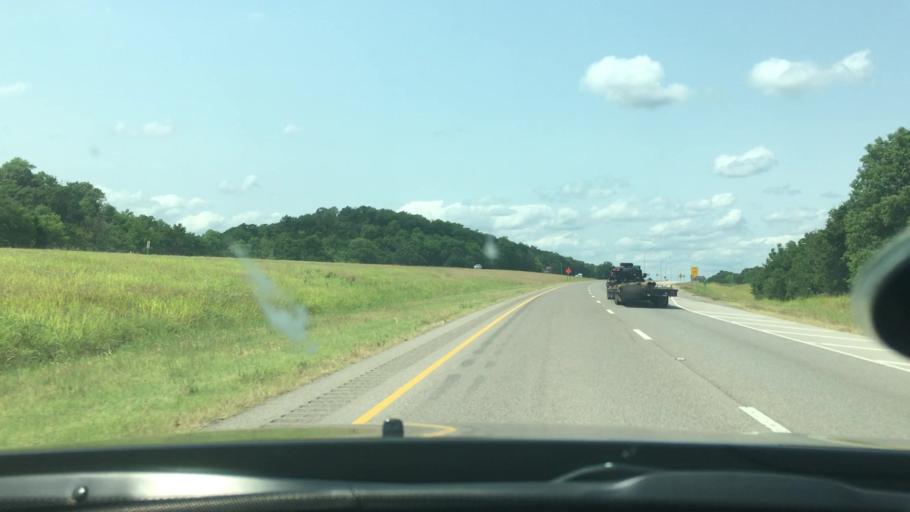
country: US
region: Oklahoma
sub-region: Murray County
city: Davis
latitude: 34.4709
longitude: -97.1538
